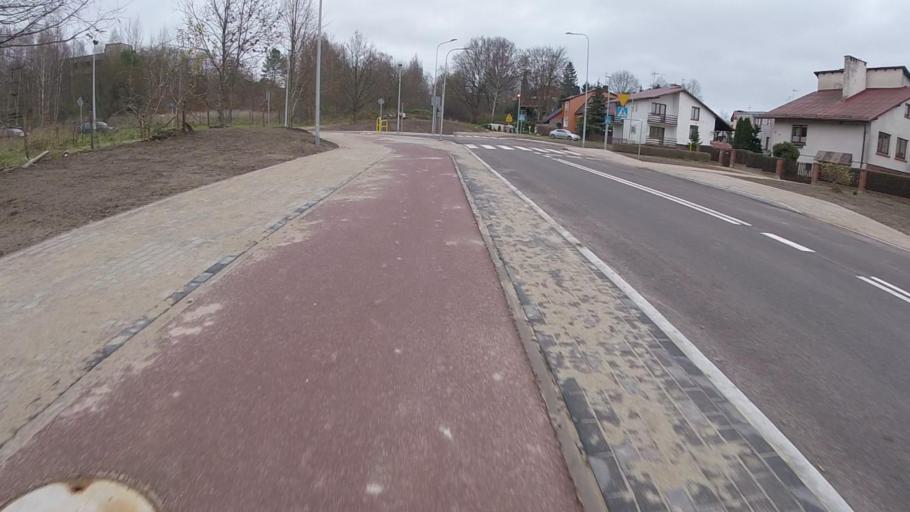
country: PL
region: West Pomeranian Voivodeship
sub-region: Koszalin
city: Koszalin
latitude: 54.1931
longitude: 16.2236
